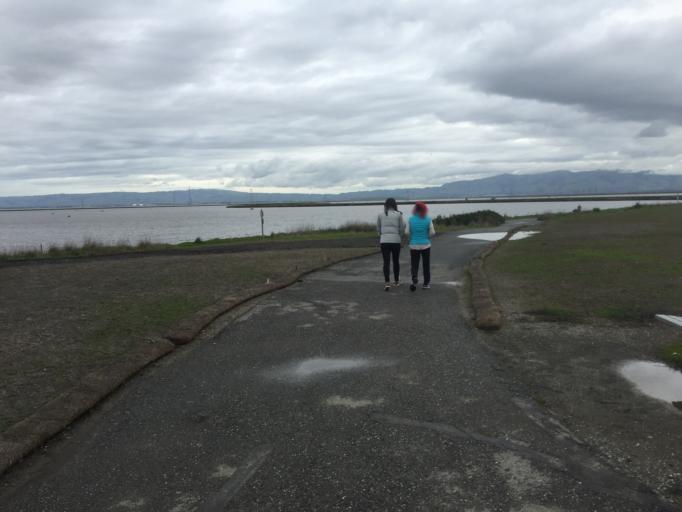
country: US
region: California
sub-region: Santa Clara County
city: Mountain View
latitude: 37.4351
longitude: -122.0913
